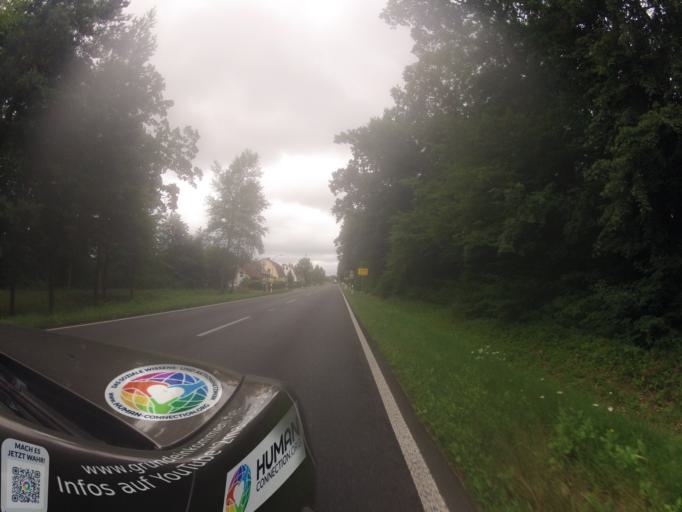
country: DE
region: Mecklenburg-Vorpommern
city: Jatznick
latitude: 53.5890
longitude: 13.9380
